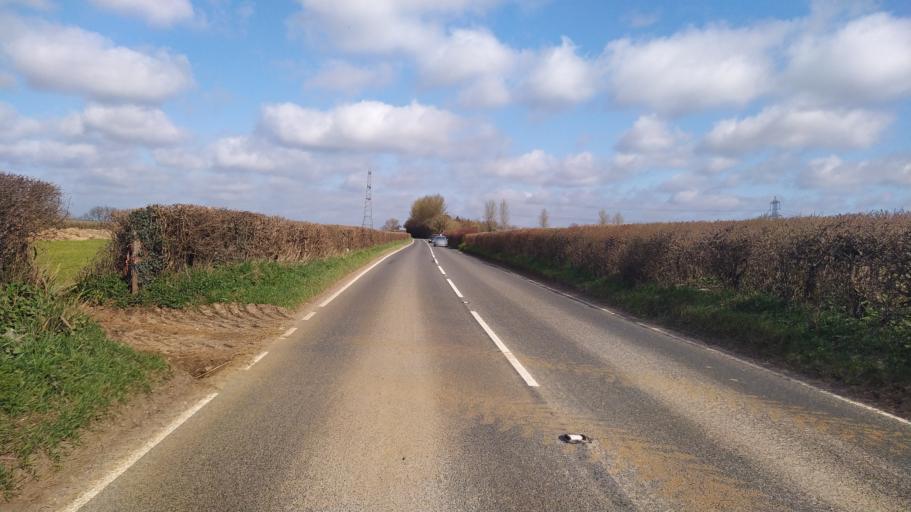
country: GB
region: England
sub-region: Dorset
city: Bridport
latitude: 50.7522
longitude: -2.7400
